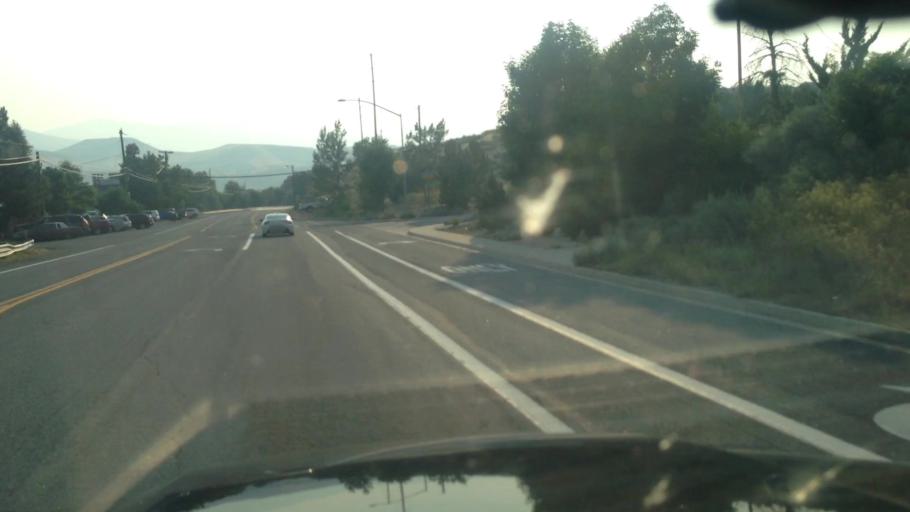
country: US
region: Nevada
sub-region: Washoe County
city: Mogul
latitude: 39.5093
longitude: -119.8885
